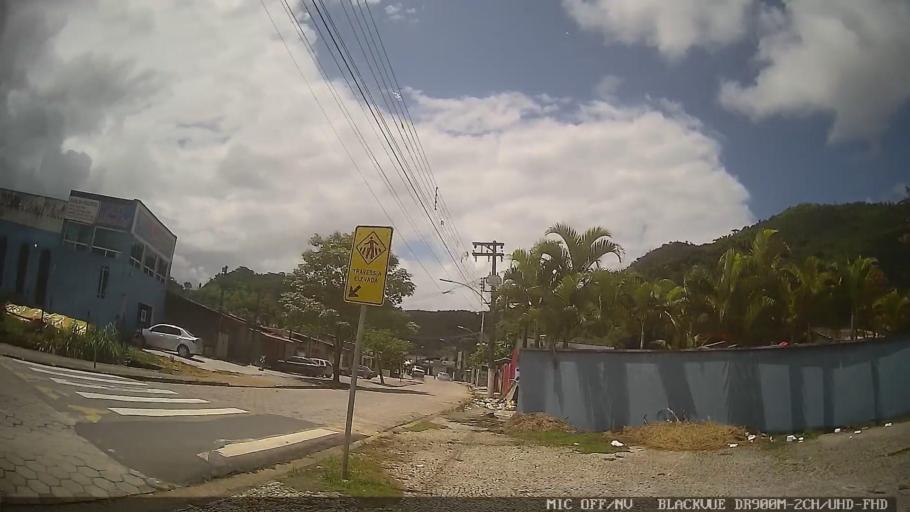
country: BR
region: Sao Paulo
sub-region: Caraguatatuba
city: Caraguatatuba
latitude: -23.6088
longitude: -45.3752
